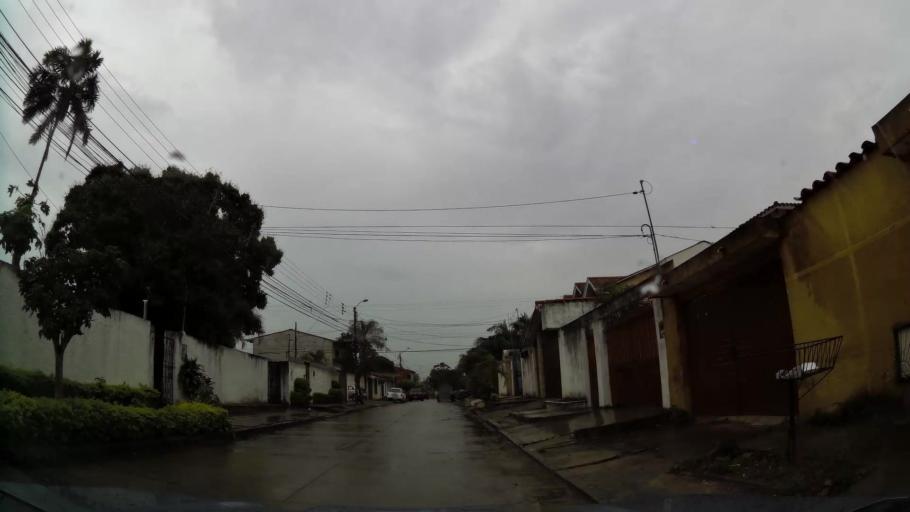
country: BO
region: Santa Cruz
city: Santa Cruz de la Sierra
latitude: -17.7920
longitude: -63.2100
